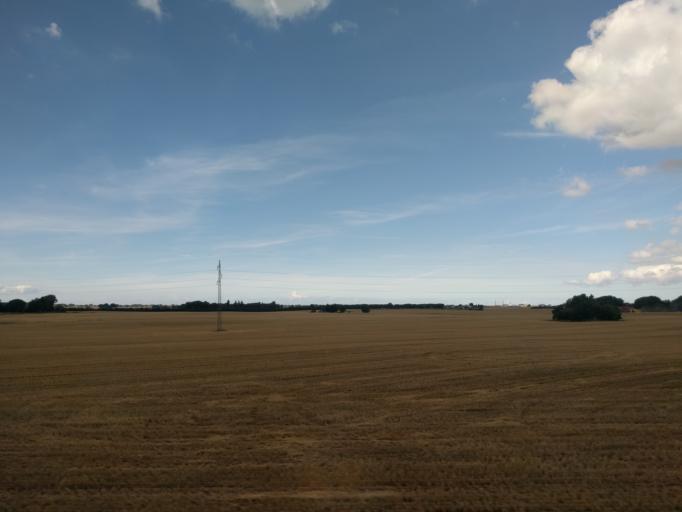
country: DK
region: Zealand
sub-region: Slagelse Kommune
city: Forlev
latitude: 55.3865
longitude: 11.2853
